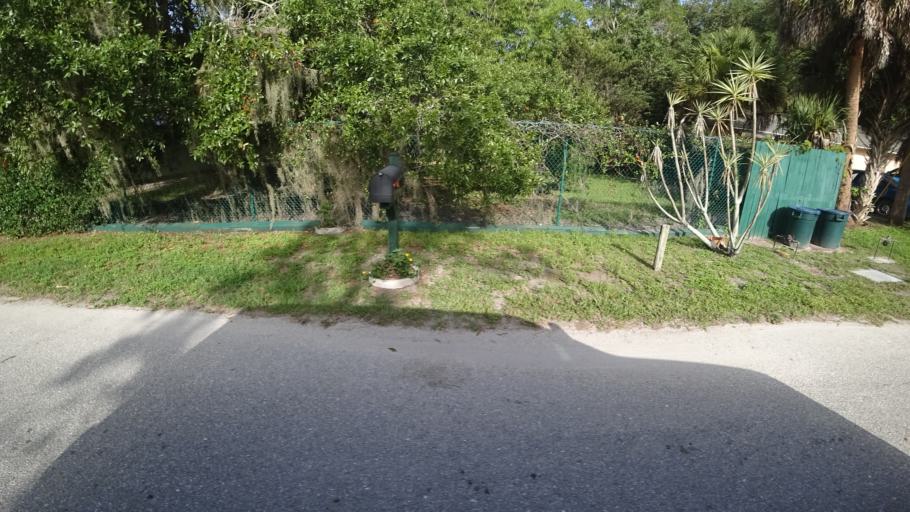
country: US
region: Florida
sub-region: Sarasota County
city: Desoto Lakes
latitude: 27.4227
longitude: -82.4751
